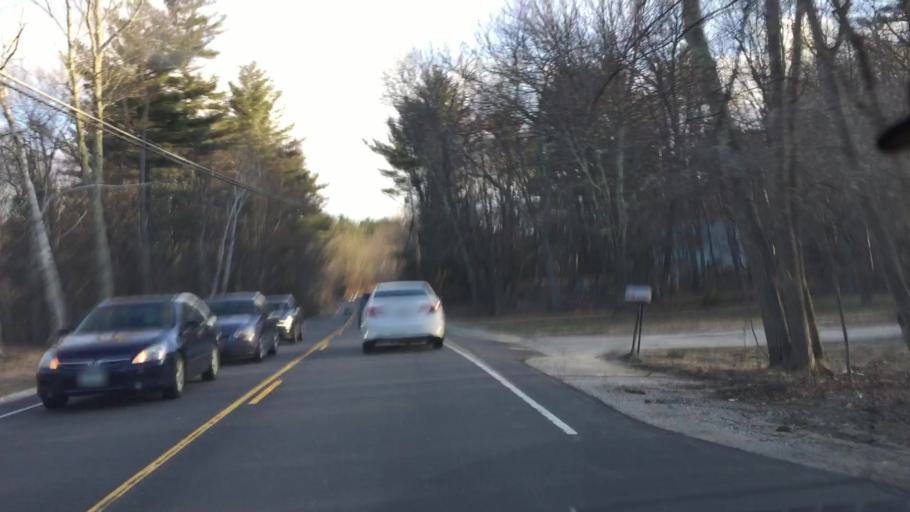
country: US
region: New Hampshire
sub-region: Rockingham County
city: Londonderry
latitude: 42.8275
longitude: -71.3654
